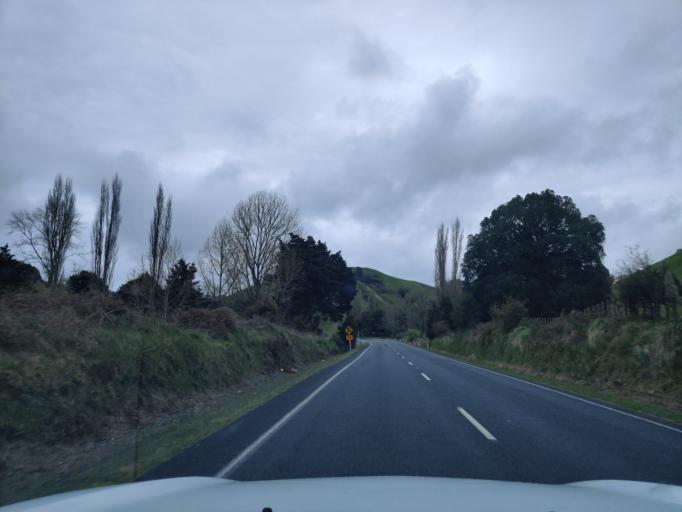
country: NZ
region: Waikato
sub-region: Otorohanga District
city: Otorohanga
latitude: -38.5668
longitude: 175.2049
